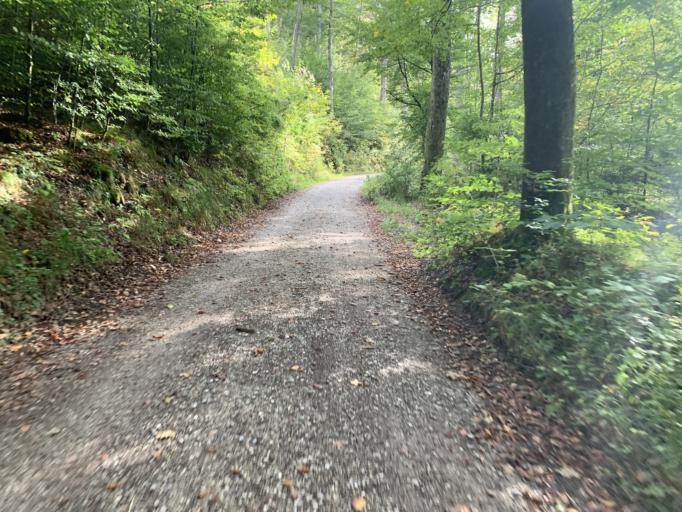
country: DE
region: Bavaria
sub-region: Upper Bavaria
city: Grunwald
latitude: 48.0329
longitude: 11.5105
